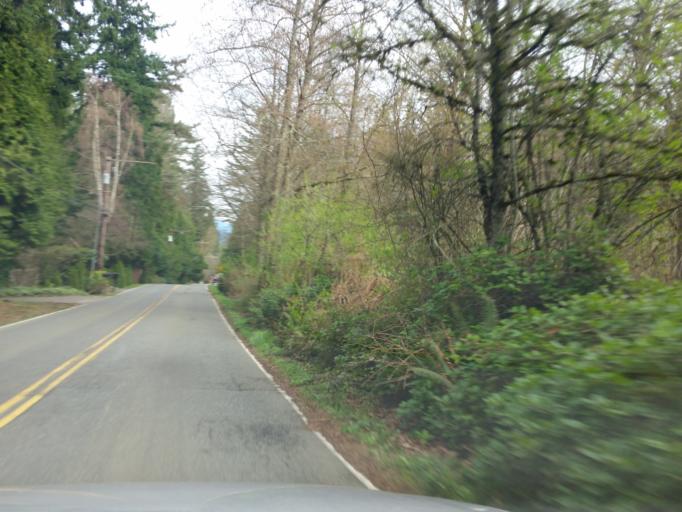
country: US
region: Washington
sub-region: King County
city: Woodinville
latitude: 47.7542
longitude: -122.1245
